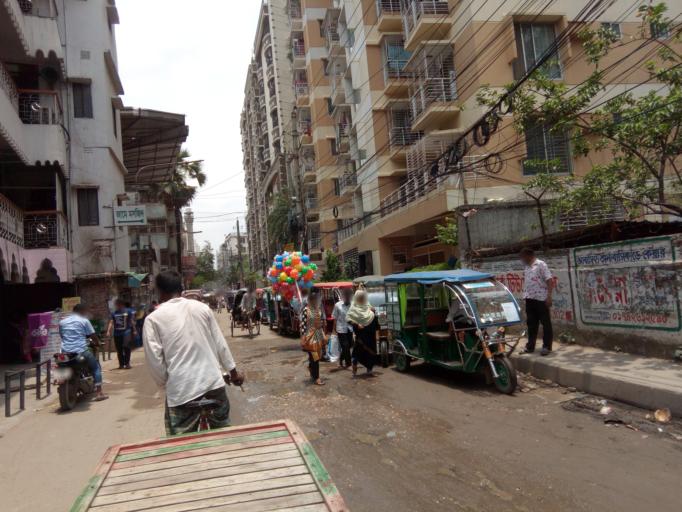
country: BD
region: Dhaka
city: Paltan
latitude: 23.7490
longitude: 90.4079
